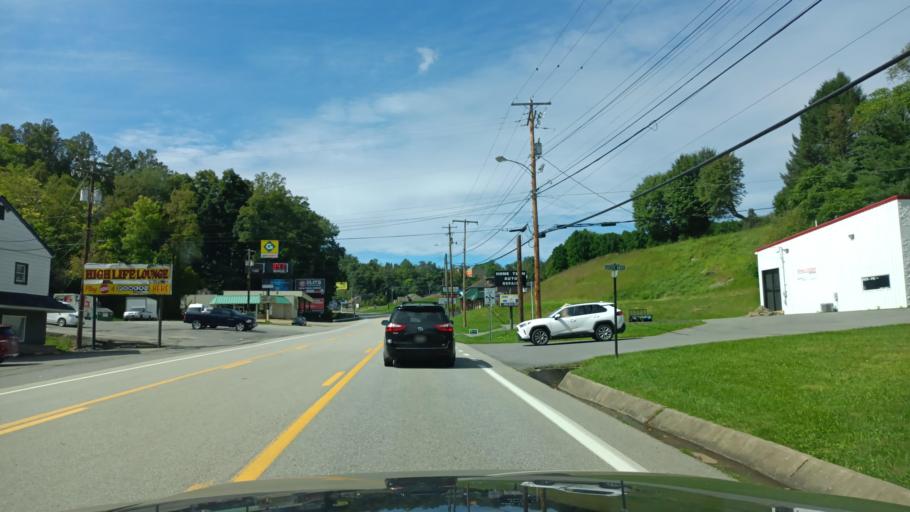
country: US
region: West Virginia
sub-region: Harrison County
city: Bridgeport
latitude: 39.2817
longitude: -80.2647
